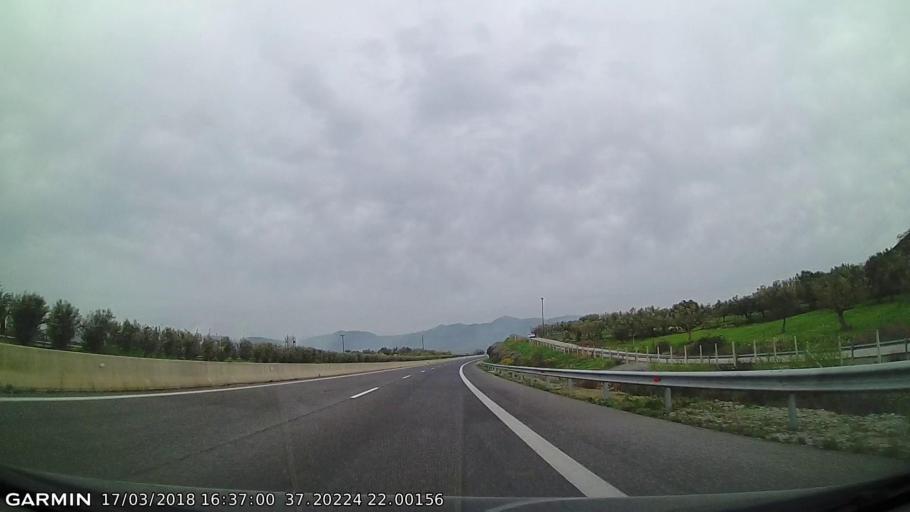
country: GR
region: Peloponnese
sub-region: Nomos Messinias
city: Meligalas
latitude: 37.2033
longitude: 22.0011
